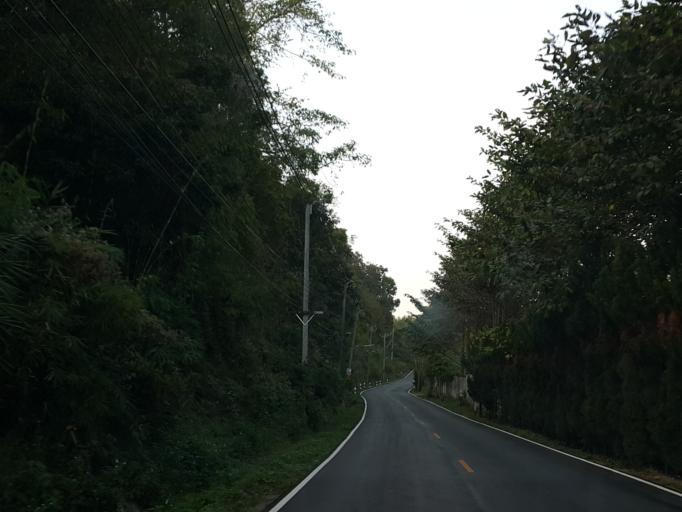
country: TH
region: Chiang Mai
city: Mae On
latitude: 18.8828
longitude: 99.2657
